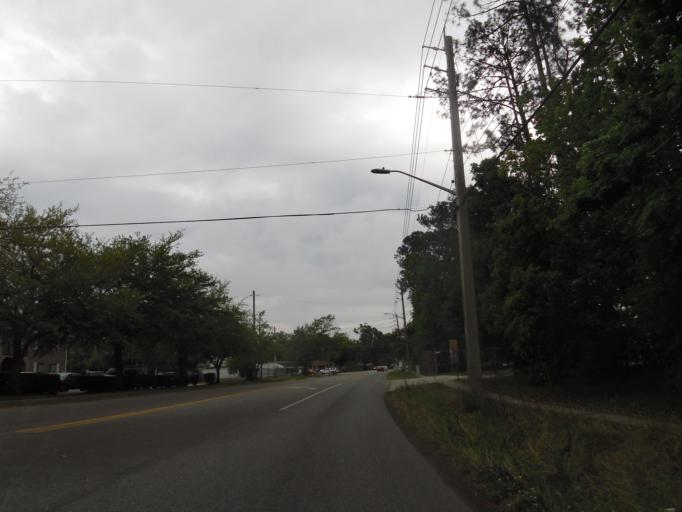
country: US
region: Florida
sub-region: Duval County
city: Jacksonville
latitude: 30.2942
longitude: -81.6271
